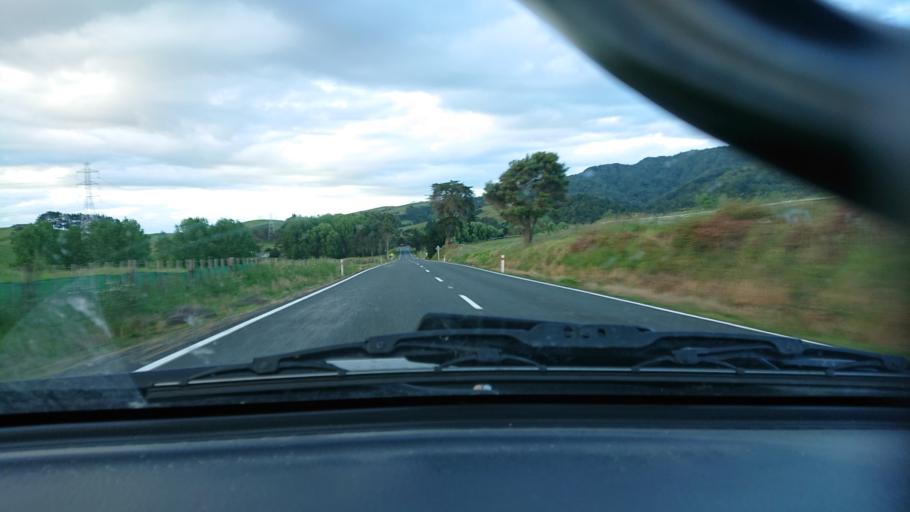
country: NZ
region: Auckland
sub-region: Auckland
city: Parakai
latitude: -36.4673
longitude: 174.4464
